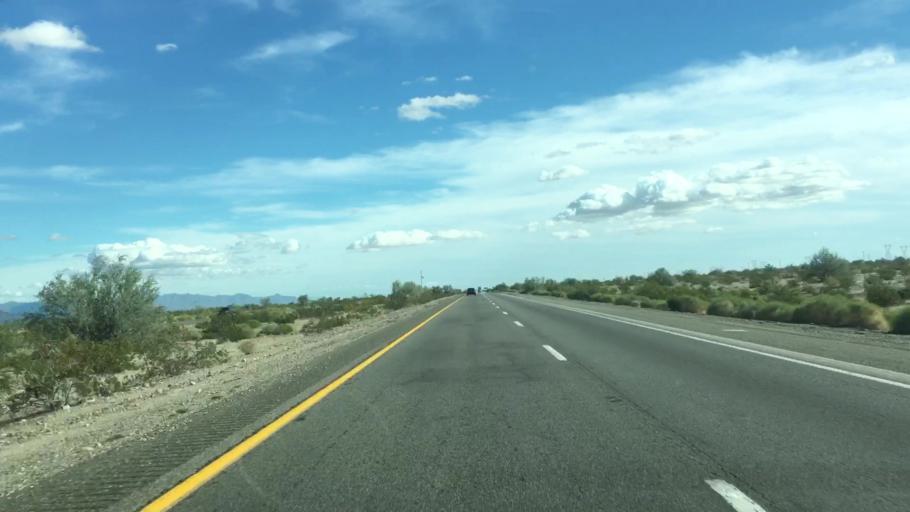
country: US
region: California
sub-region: Imperial County
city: Niland
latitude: 33.6960
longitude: -115.2899
